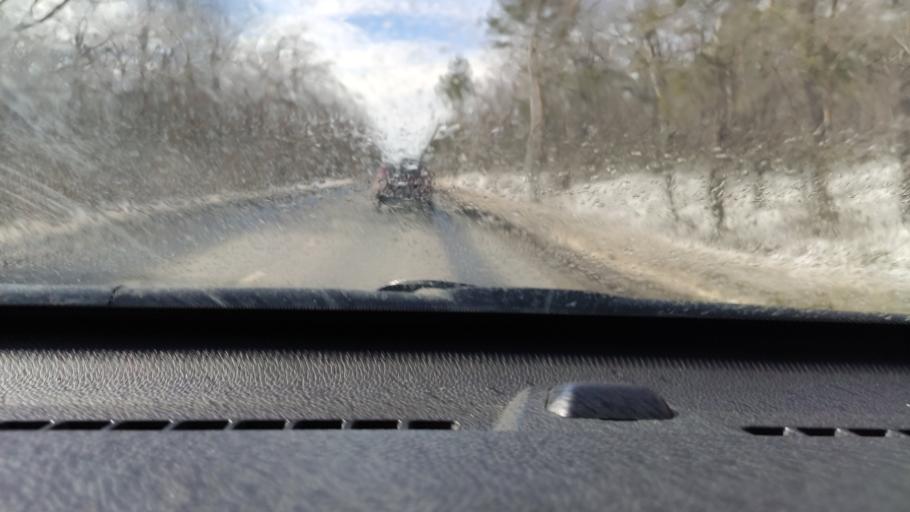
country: RU
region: Samara
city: Tol'yatti
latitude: 53.4736
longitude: 49.3947
